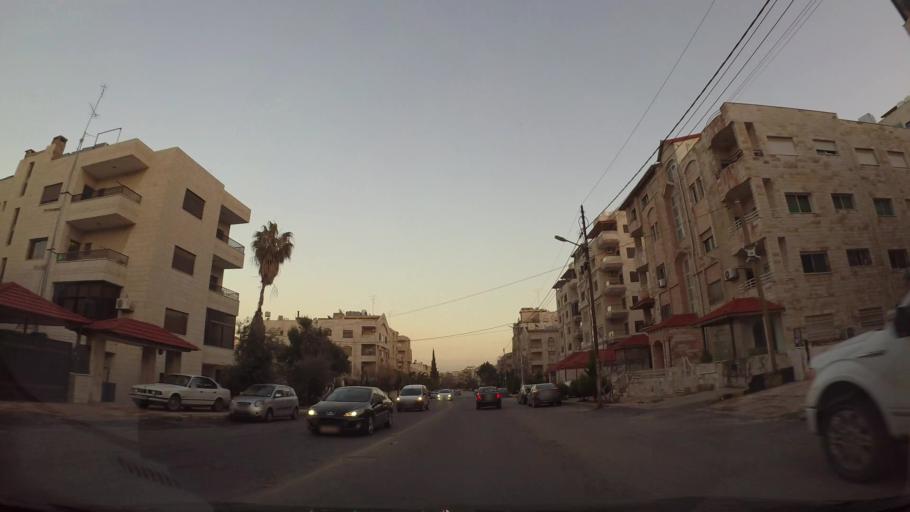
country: JO
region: Amman
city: Al Jubayhah
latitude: 31.9896
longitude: 35.8798
